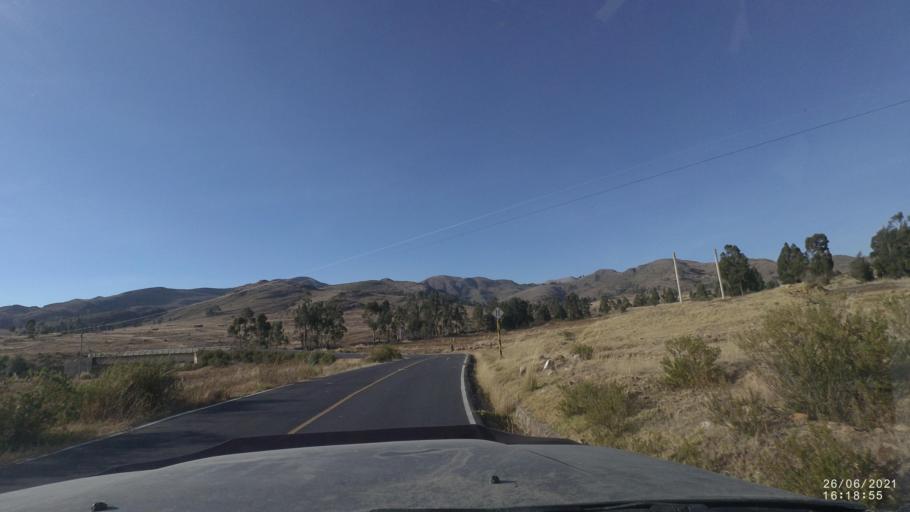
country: BO
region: Cochabamba
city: Arani
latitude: -17.7991
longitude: -65.8015
